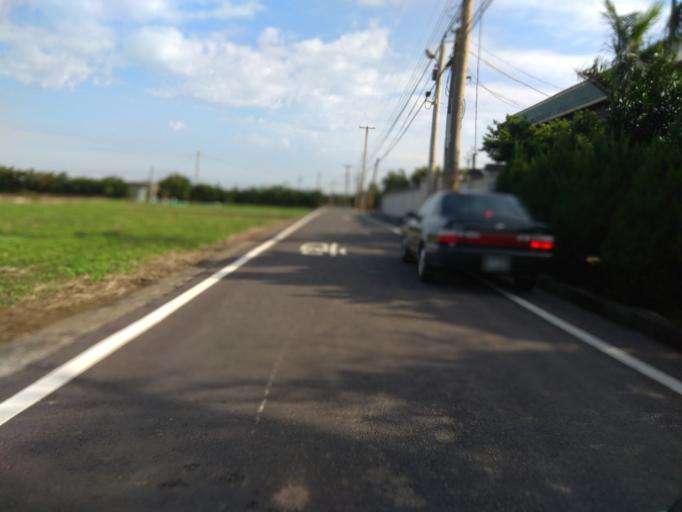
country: TW
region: Taiwan
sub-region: Hsinchu
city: Zhubei
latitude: 25.0020
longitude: 121.0463
